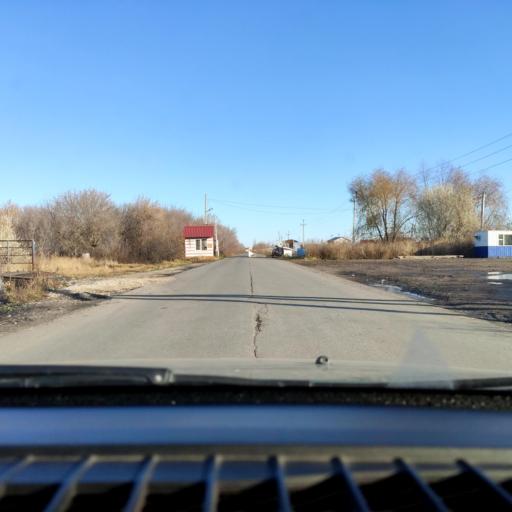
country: RU
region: Samara
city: Tol'yatti
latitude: 53.6590
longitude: 49.3326
